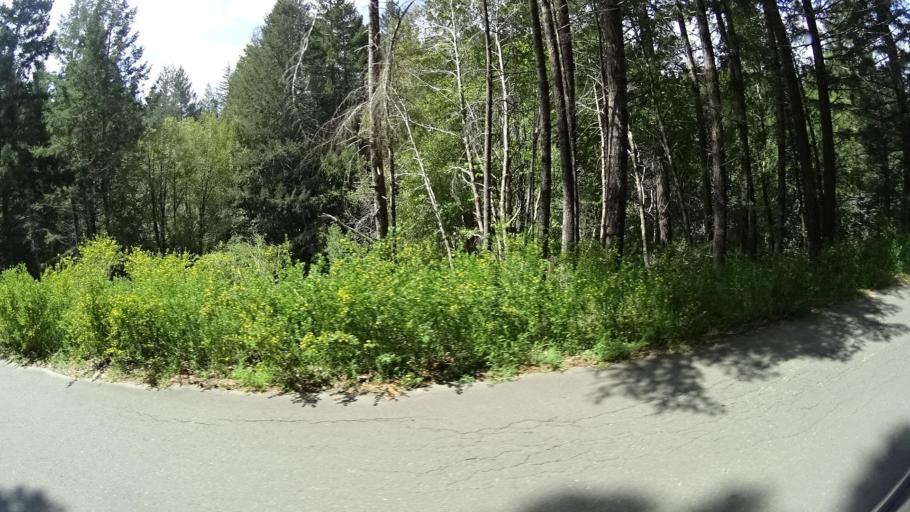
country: US
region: California
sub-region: Humboldt County
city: Redway
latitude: 40.0496
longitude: -123.9575
